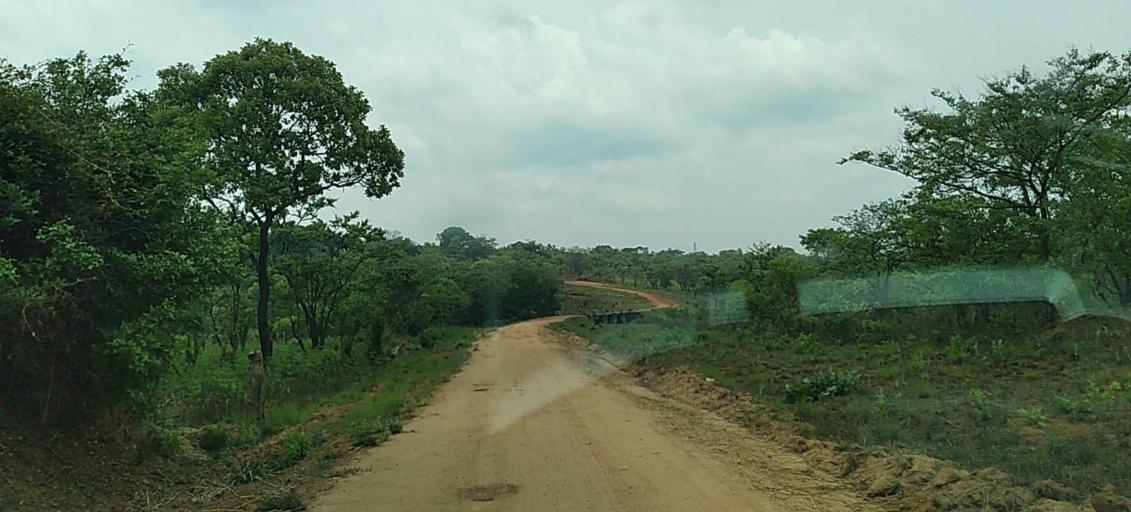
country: ZM
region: North-Western
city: Mwinilunga
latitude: -11.4594
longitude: 24.7599
